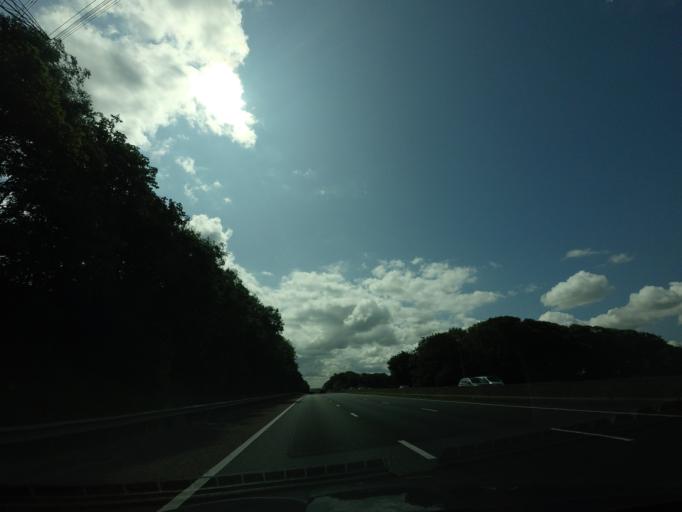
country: GB
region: England
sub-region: Lancashire
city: Lancaster
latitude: 54.0183
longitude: -2.7825
